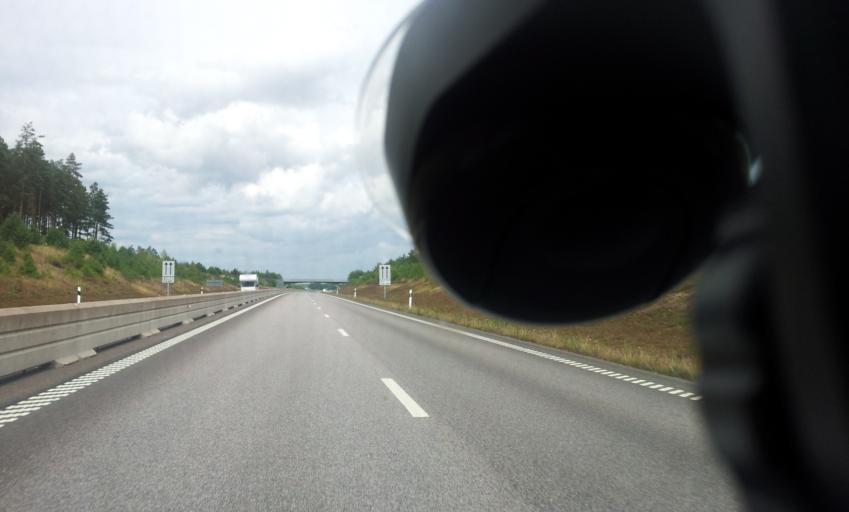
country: SE
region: Kalmar
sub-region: Kalmar Kommun
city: Ljungbyholm
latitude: 56.5964
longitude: 16.1265
